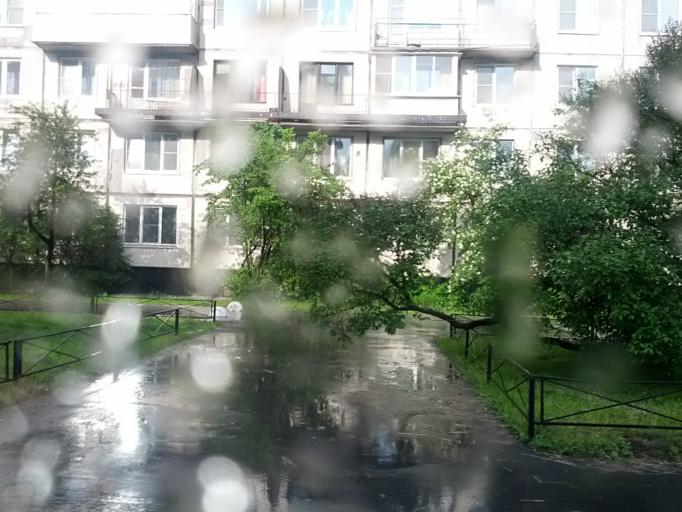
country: RU
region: St.-Petersburg
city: Obukhovo
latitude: 59.8935
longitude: 30.4783
